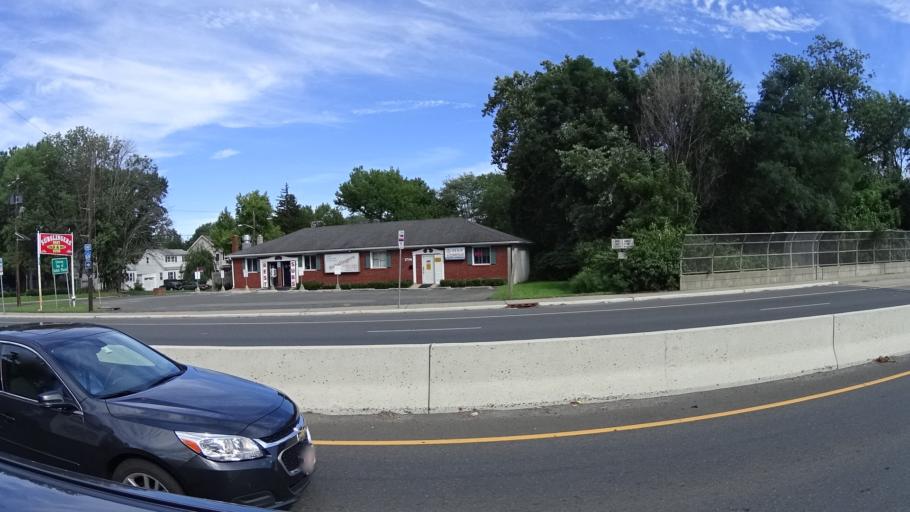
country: US
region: New Jersey
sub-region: Union County
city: Plainfield
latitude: 40.6496
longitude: -74.4067
